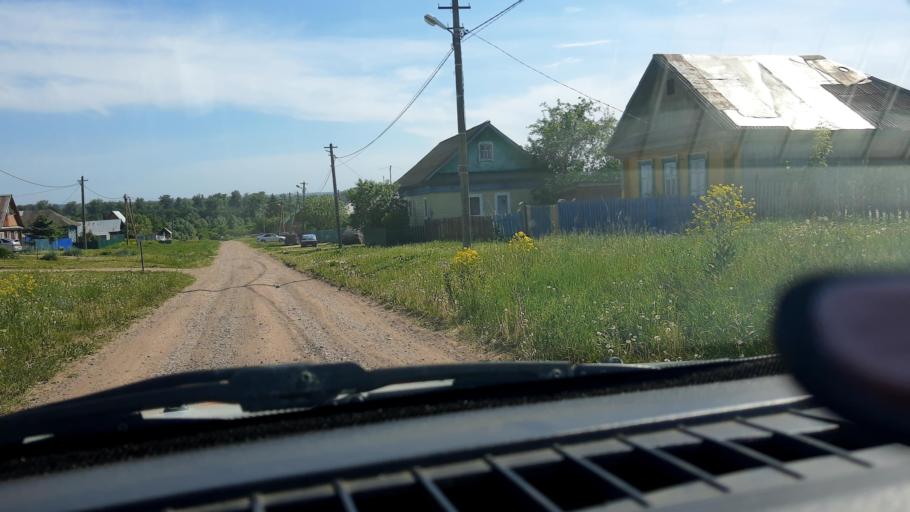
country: RU
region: Bashkortostan
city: Iglino
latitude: 54.8827
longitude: 56.3063
